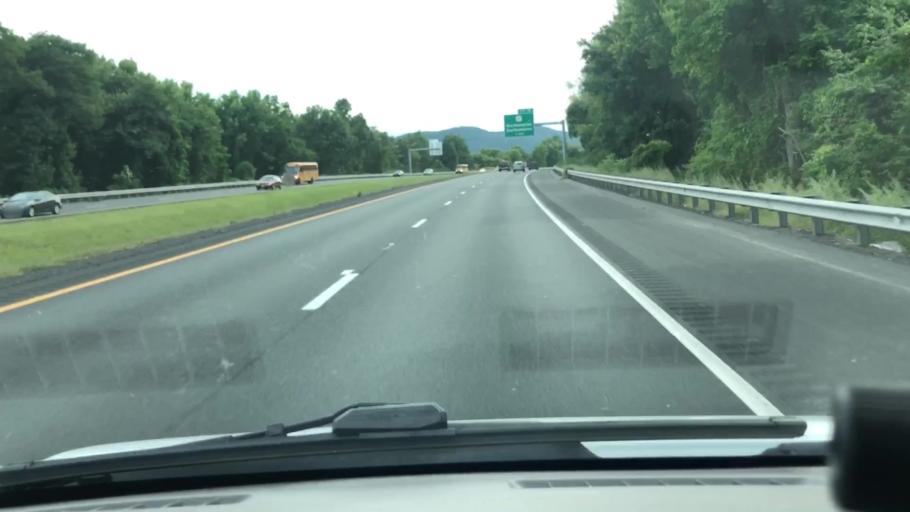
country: US
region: Massachusetts
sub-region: Hampshire County
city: Northampton
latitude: 42.3198
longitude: -72.6158
